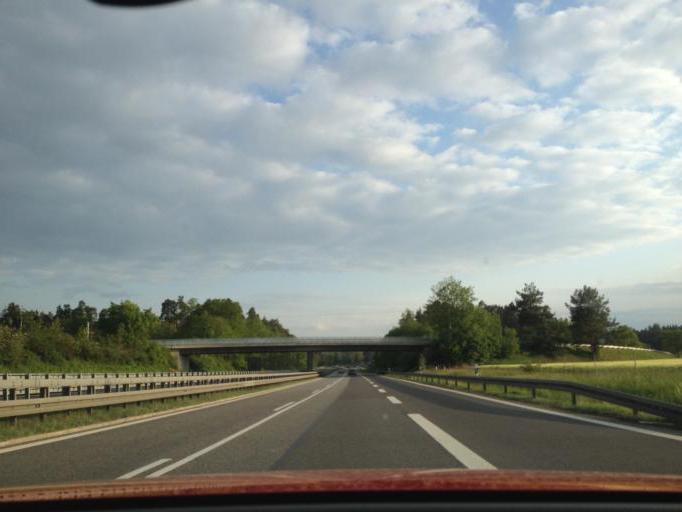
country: DE
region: Bavaria
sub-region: Upper Palatinate
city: Neustadt an der Waldnaab
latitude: 49.7218
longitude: 12.1511
